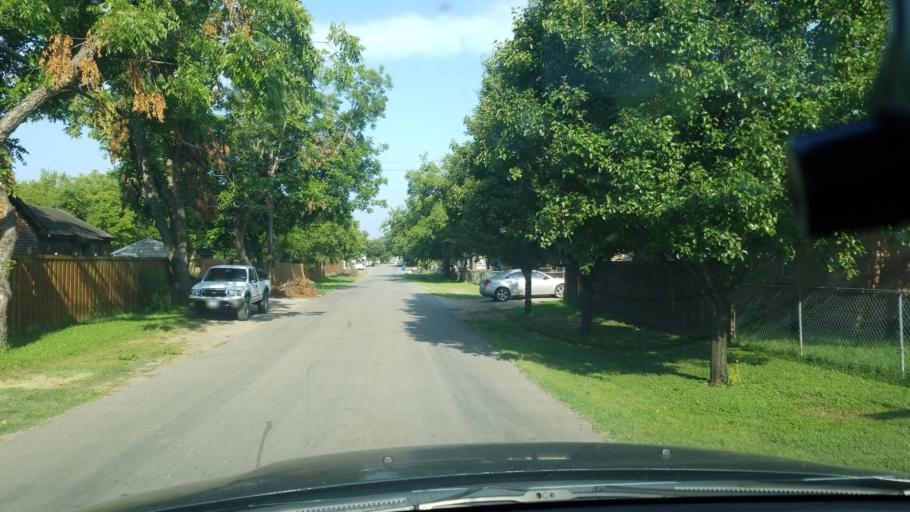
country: US
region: Texas
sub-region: Dallas County
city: Balch Springs
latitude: 32.7289
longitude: -96.6848
